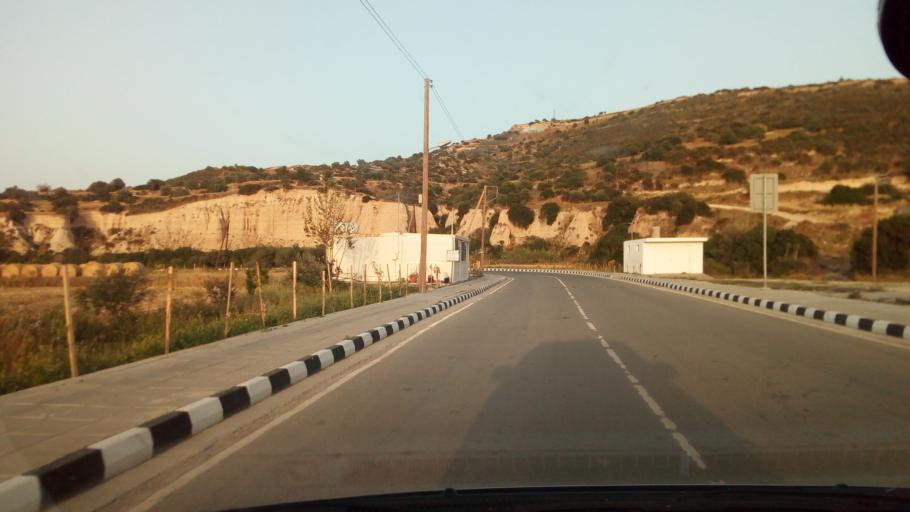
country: CY
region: Larnaka
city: Kofinou
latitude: 34.7963
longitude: 33.3857
